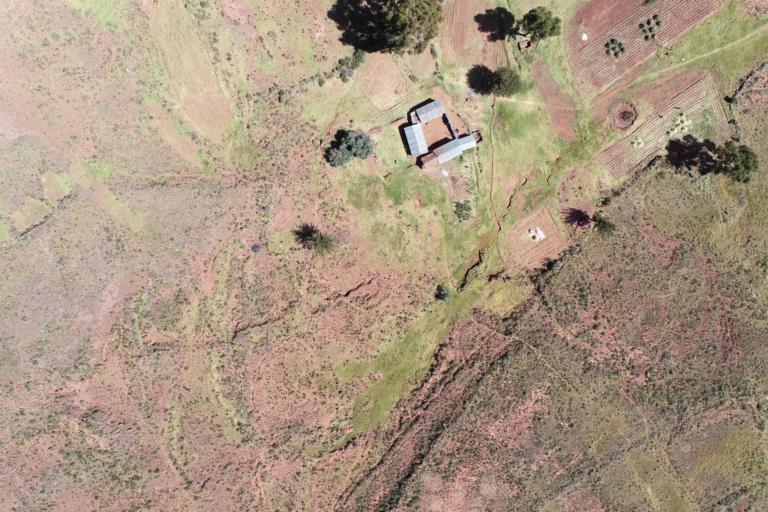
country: BO
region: La Paz
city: Tiahuanaco
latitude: -16.6047
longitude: -68.7781
